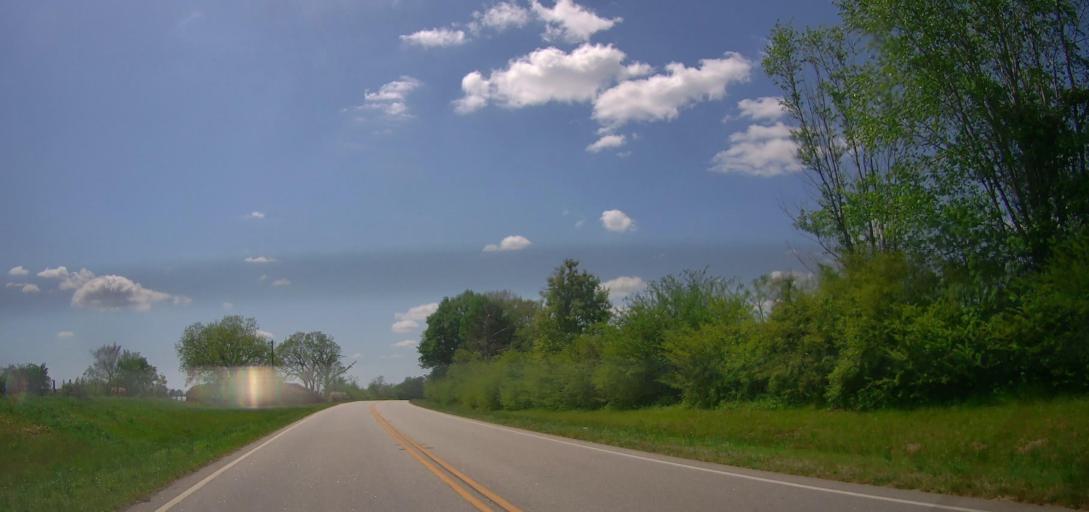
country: US
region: Georgia
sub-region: Putnam County
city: Eatonton
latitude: 33.3383
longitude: -83.3263
